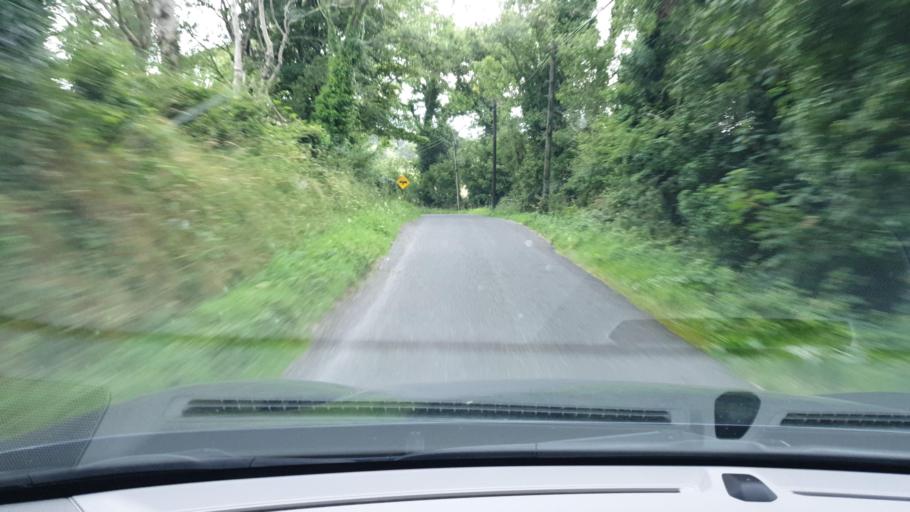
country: IE
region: Leinster
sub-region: Wicklow
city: Blessington
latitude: 53.2296
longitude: -6.5185
